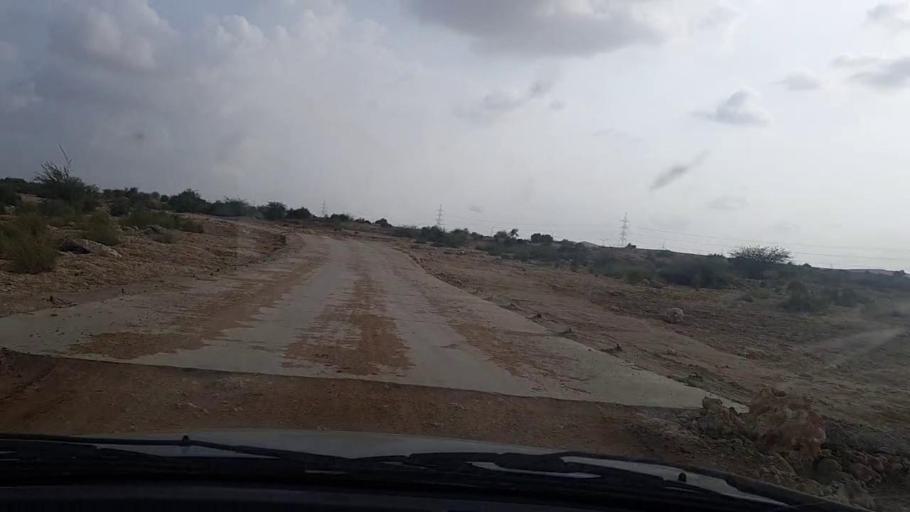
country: PK
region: Sindh
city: Thatta
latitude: 25.0734
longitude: 67.8910
